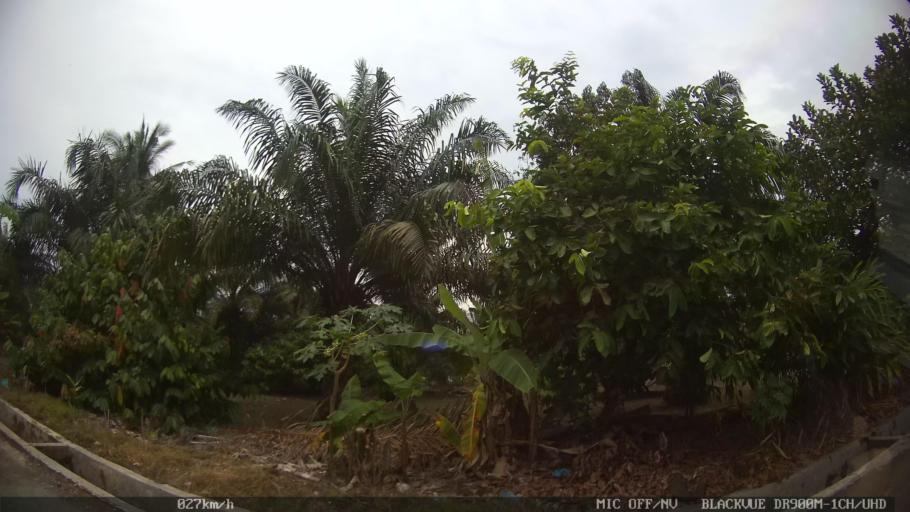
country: ID
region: North Sumatra
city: Sunggal
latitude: 3.6042
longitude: 98.5541
